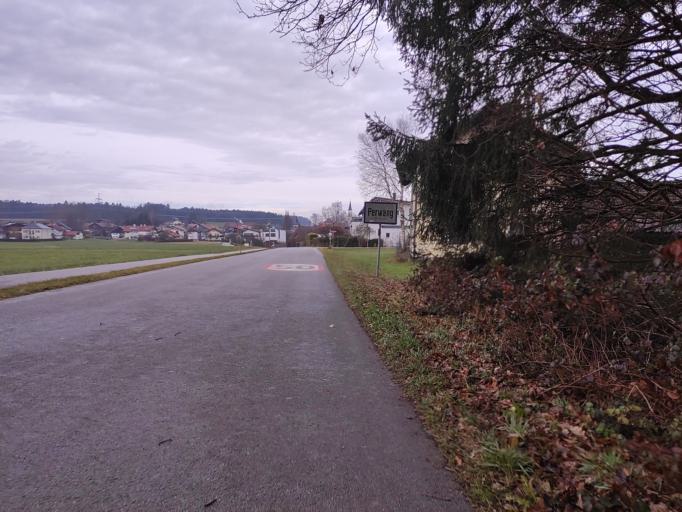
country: AT
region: Salzburg
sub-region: Politischer Bezirk Salzburg-Umgebung
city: Berndorf bei Salzburg
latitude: 48.0046
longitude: 13.0876
